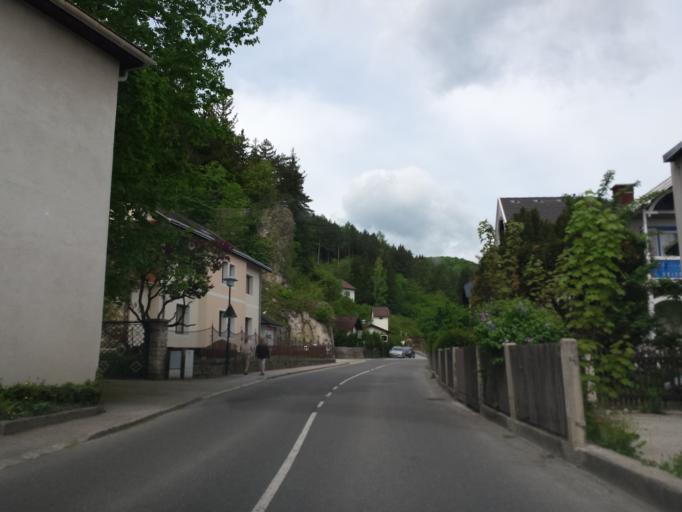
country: AT
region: Lower Austria
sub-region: Politischer Bezirk Wiener Neustadt
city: Pernitz
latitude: 47.9000
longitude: 15.9556
